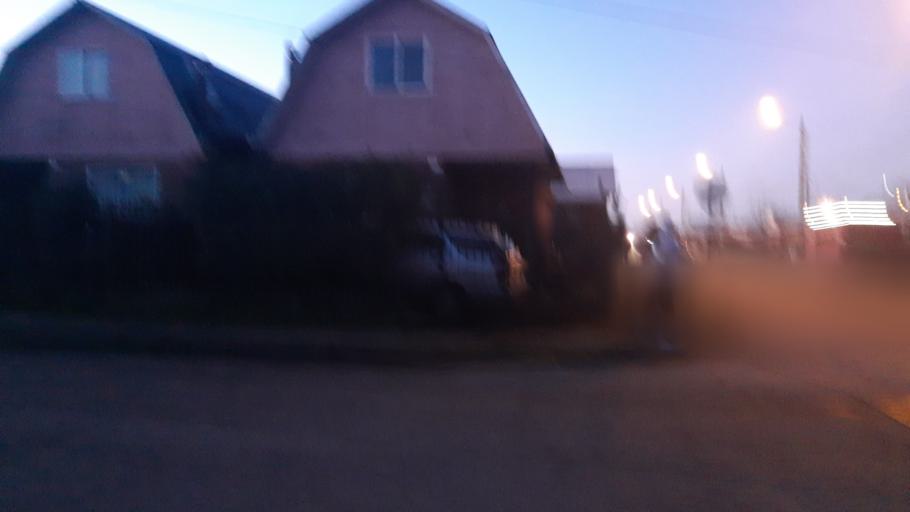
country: CL
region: Araucania
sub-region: Provincia de Cautin
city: Villarrica
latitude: -39.3078
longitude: -72.2150
